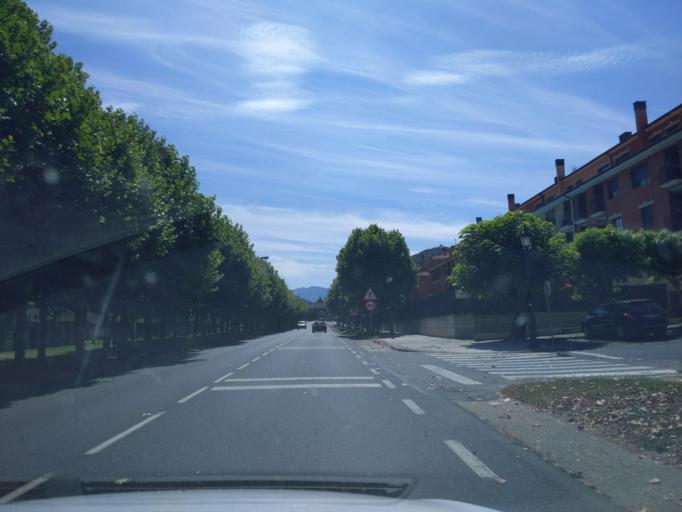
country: ES
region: La Rioja
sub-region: Provincia de La Rioja
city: Ezcaray
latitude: 42.3311
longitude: -3.0132
